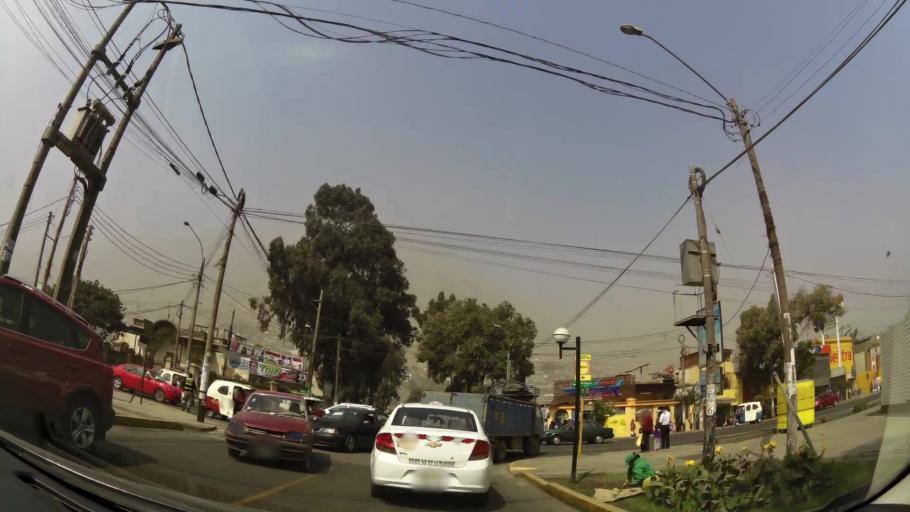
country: PE
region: Lima
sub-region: Lima
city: Asentamiento Humano Nicolas de Pierola
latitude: -11.9384
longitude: -76.6978
